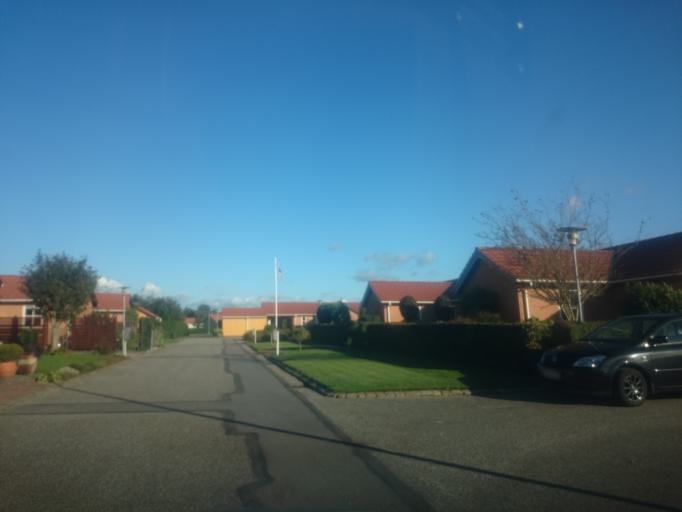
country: DK
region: South Denmark
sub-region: Billund Kommune
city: Billund
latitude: 55.7192
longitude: 9.1209
